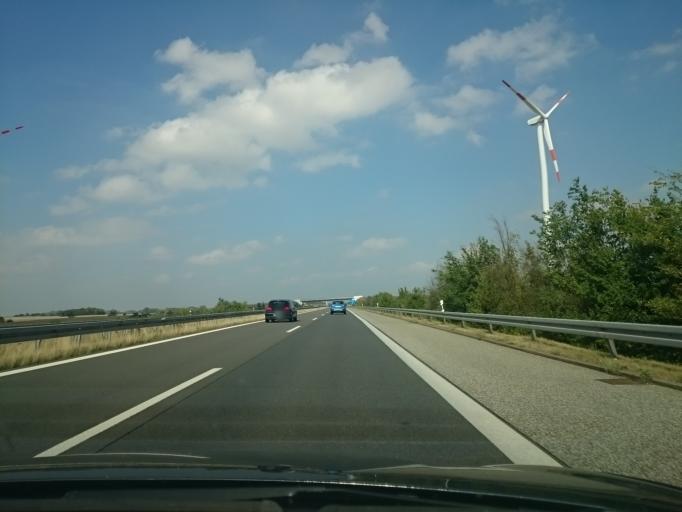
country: DE
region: Brandenburg
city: Schonfeld
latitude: 53.3878
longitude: 13.9910
